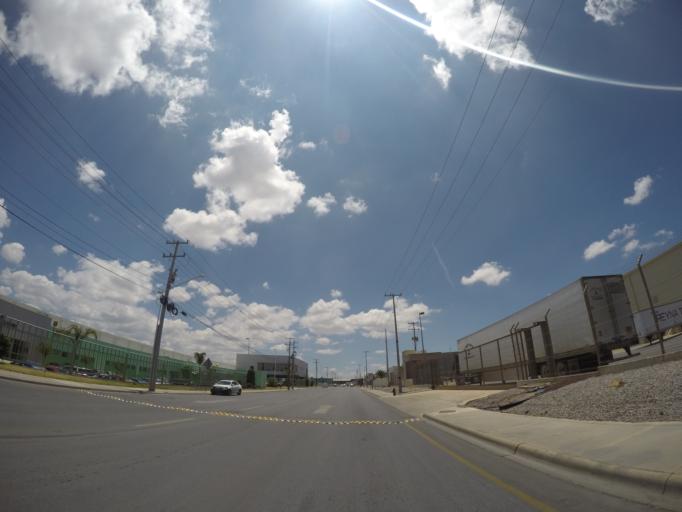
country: MX
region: San Luis Potosi
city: La Pila
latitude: 22.0392
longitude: -100.8916
